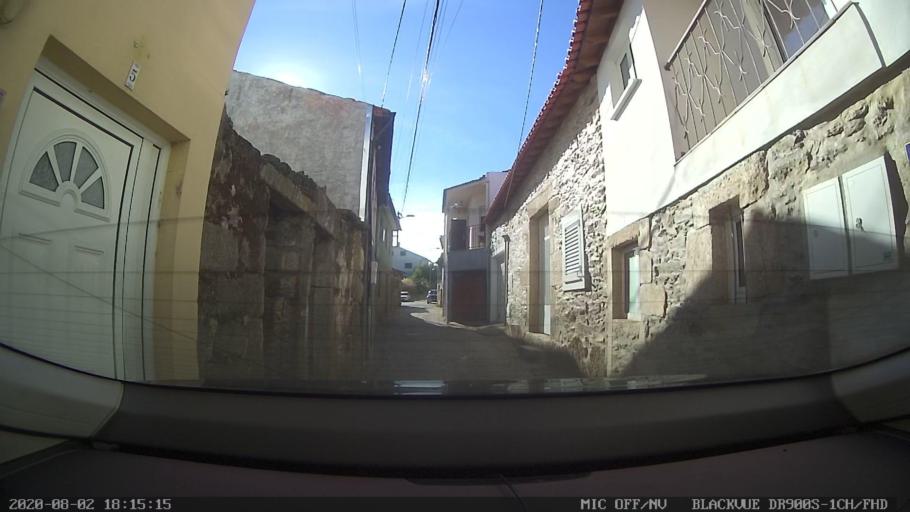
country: PT
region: Vila Real
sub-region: Murca
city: Murca
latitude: 41.4084
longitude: -7.4546
